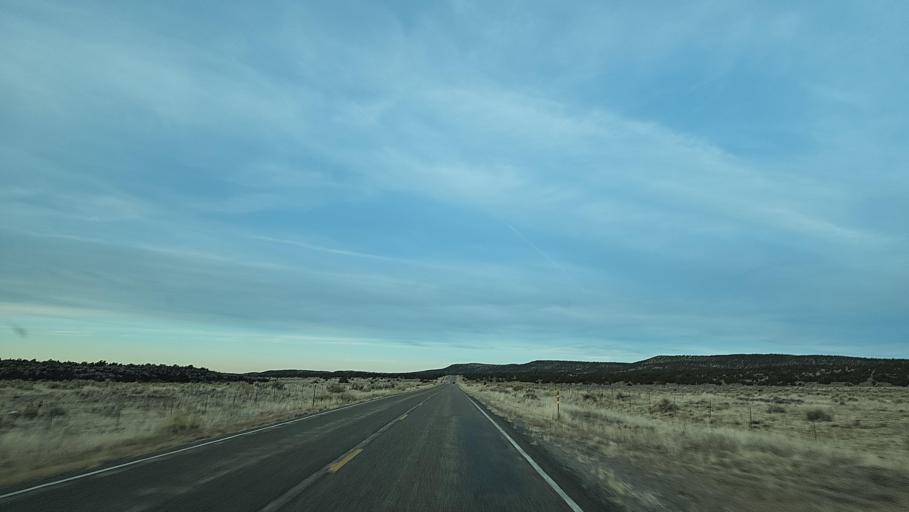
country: US
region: New Mexico
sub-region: Cibola County
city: Grants
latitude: 34.7139
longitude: -107.9864
